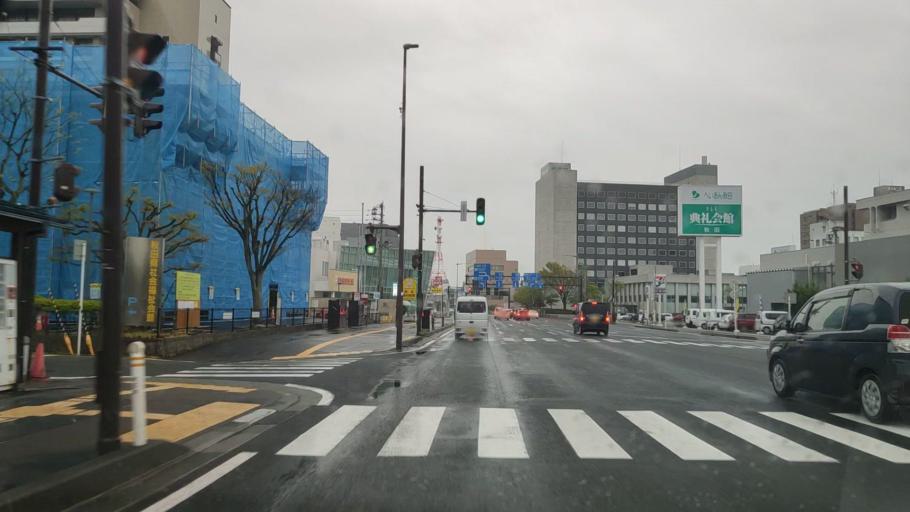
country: JP
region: Akita
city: Akita Shi
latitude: 39.7208
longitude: 140.1086
